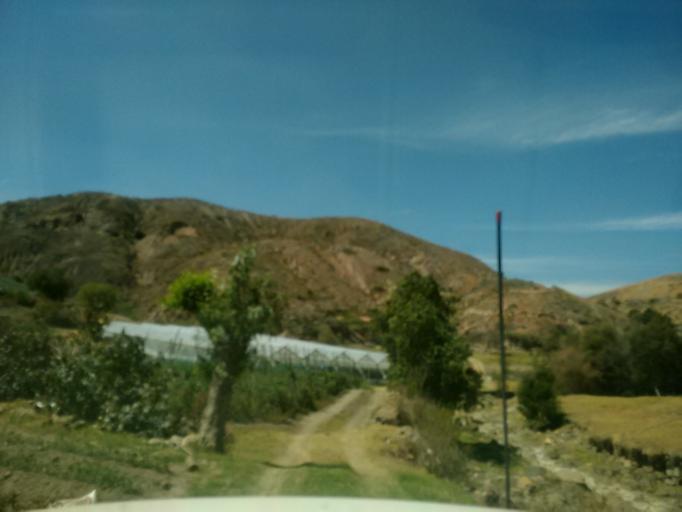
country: CO
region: Boyaca
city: Sachica
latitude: 5.5829
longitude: -73.5111
